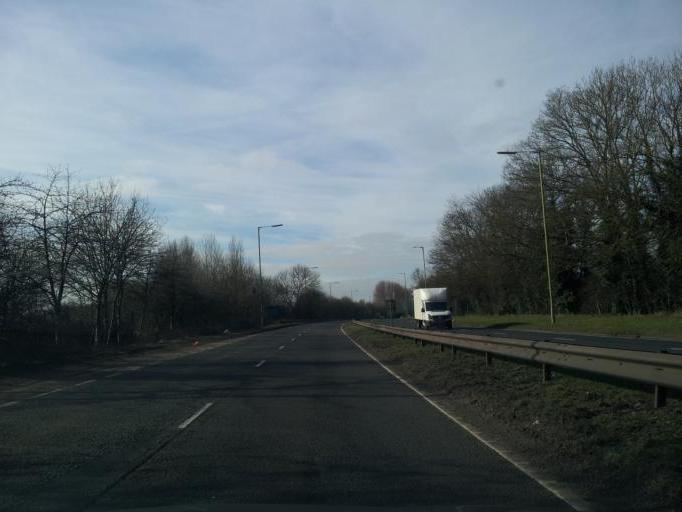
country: GB
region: England
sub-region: Hertfordshire
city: Hatfield
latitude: 51.7508
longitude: -0.2489
